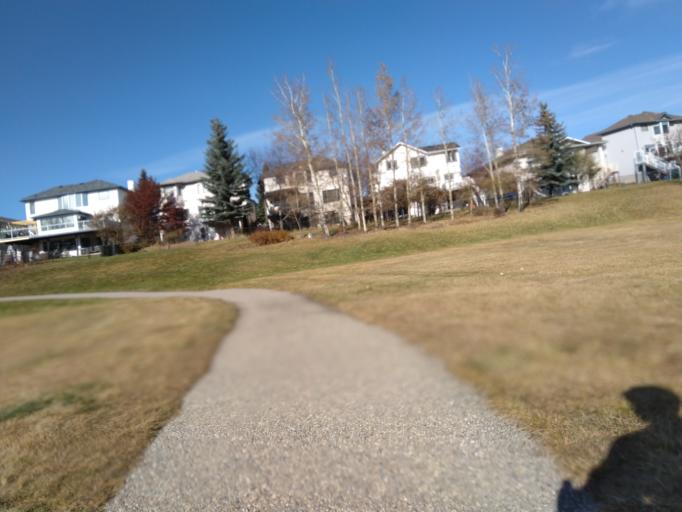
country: CA
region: Alberta
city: Calgary
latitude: 51.1489
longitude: -114.1133
